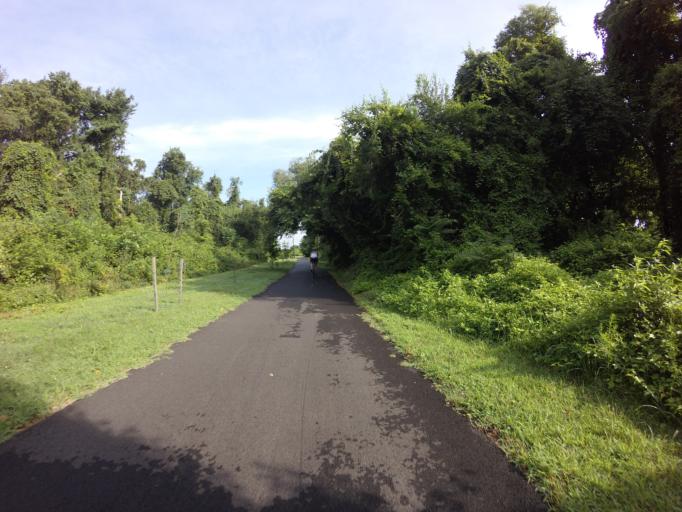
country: US
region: Maryland
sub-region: Anne Arundel County
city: Pasadena
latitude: 39.1218
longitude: -76.5902
